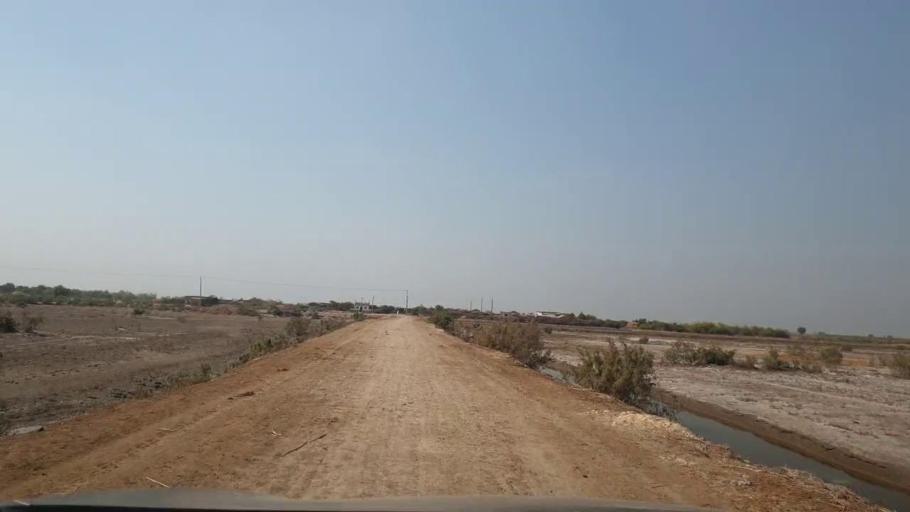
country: PK
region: Sindh
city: Berani
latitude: 25.6629
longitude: 68.8699
